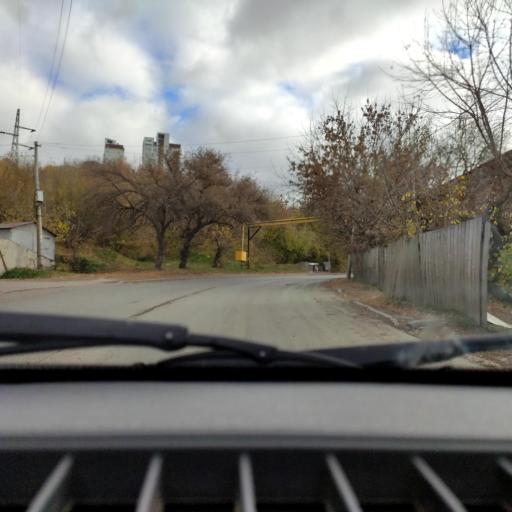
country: RU
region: Bashkortostan
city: Ufa
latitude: 54.7431
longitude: 55.9365
